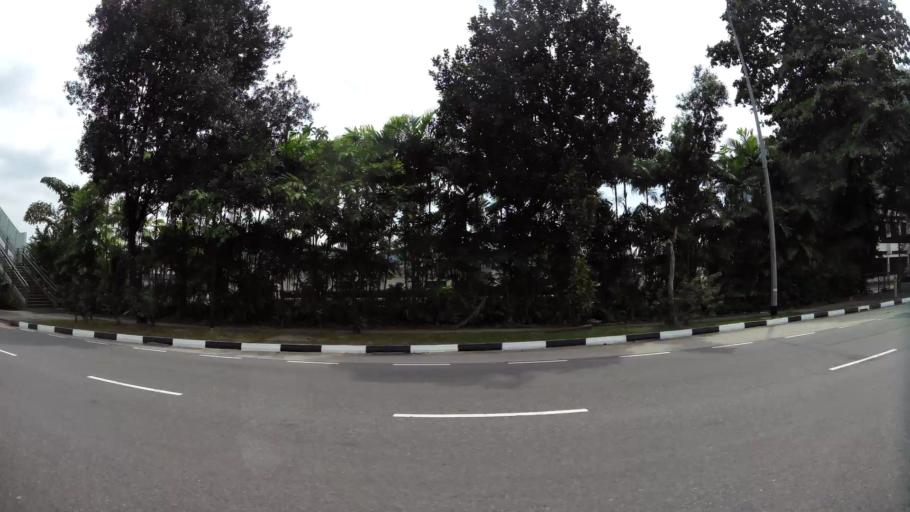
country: SG
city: Singapore
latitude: 1.3138
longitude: 103.7038
